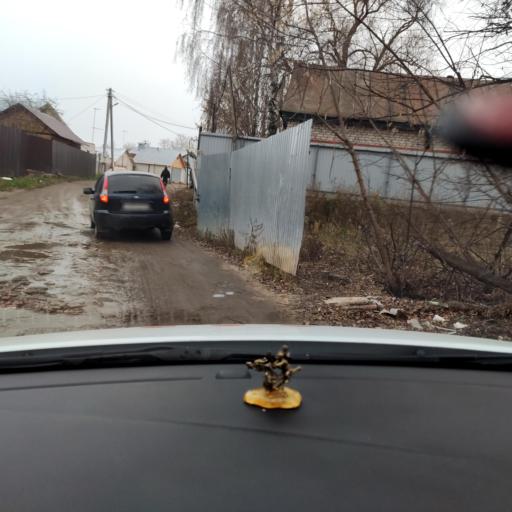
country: RU
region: Tatarstan
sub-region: Gorod Kazan'
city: Kazan
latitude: 55.8475
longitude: 49.1570
